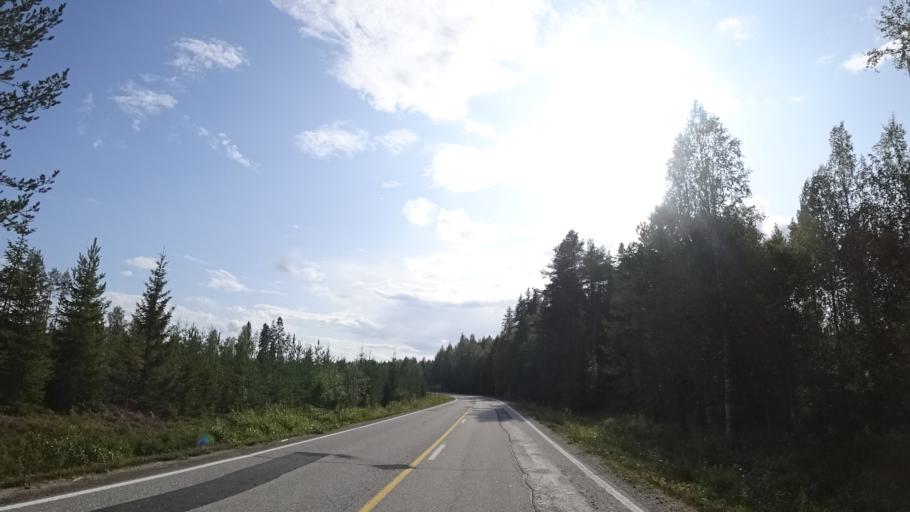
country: FI
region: North Karelia
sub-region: Pielisen Karjala
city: Lieksa
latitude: 63.4180
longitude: 30.1032
